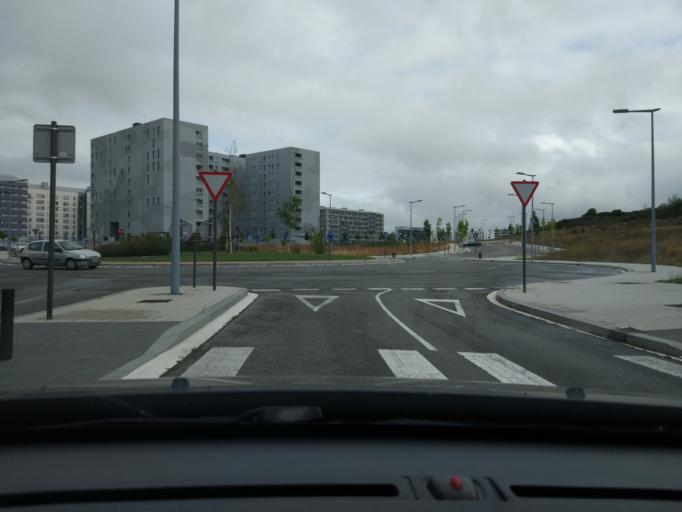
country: ES
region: Basque Country
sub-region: Provincia de Alava
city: Gasteiz / Vitoria
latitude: 42.8416
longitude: -2.6446
